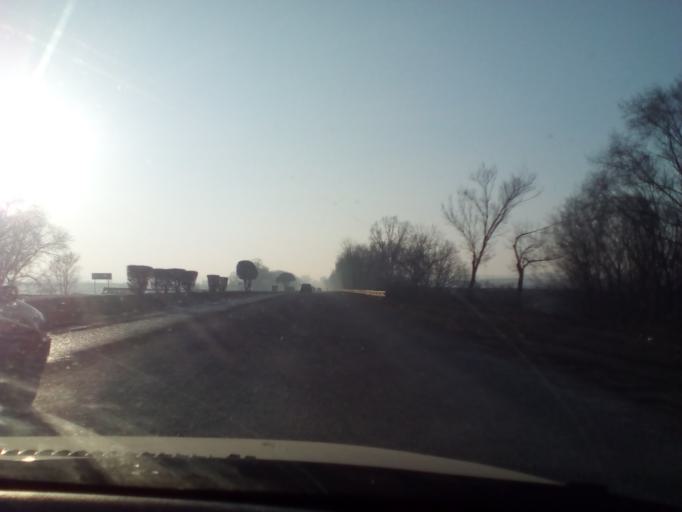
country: KZ
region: Almaty Oblysy
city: Burunday
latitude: 43.2234
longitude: 76.5956
